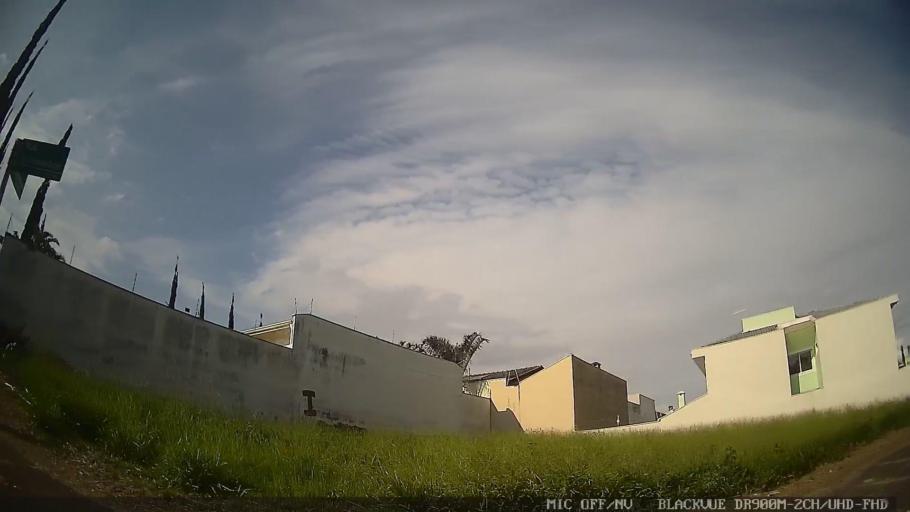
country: BR
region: Sao Paulo
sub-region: Indaiatuba
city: Indaiatuba
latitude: -23.0882
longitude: -47.2287
